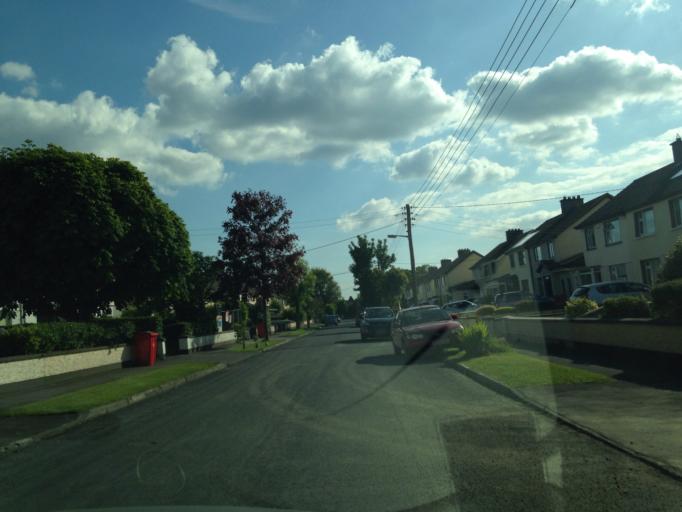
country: IE
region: Connaught
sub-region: County Galway
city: Gaillimh
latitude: 53.2742
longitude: -9.0262
